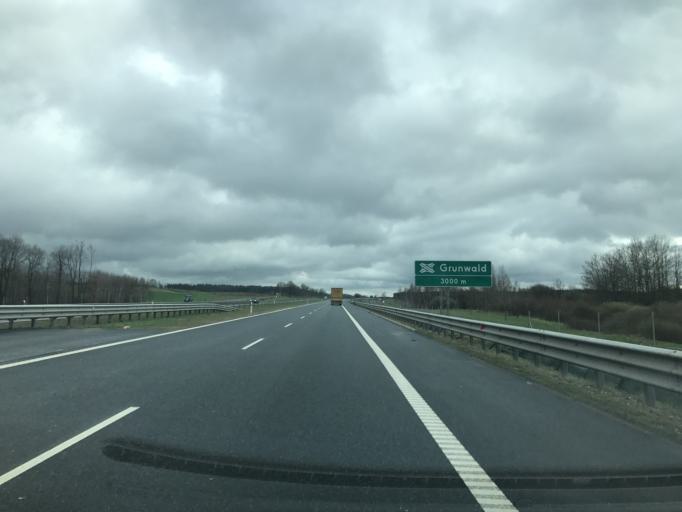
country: PL
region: Warmian-Masurian Voivodeship
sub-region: Powiat olsztynski
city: Olsztynek
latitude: 53.5602
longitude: 20.2660
